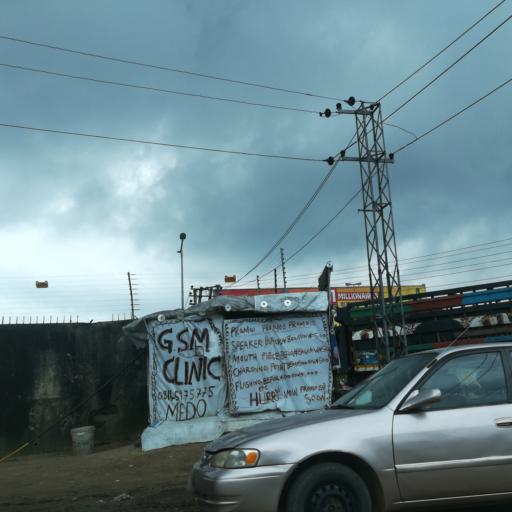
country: NG
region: Rivers
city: Port Harcourt
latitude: 4.8253
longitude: 7.0386
